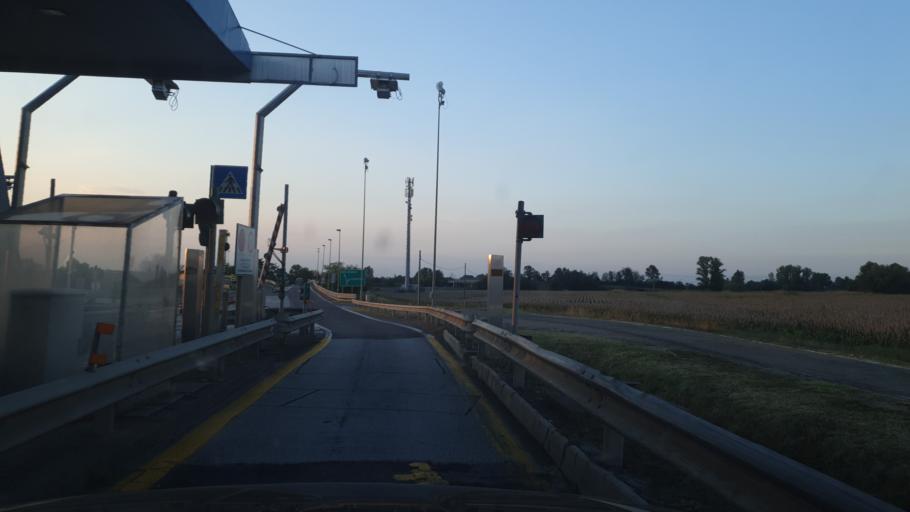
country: IT
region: Emilia-Romagna
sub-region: Provincia di Bologna
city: Progresso
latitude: 44.5885
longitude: 11.4023
